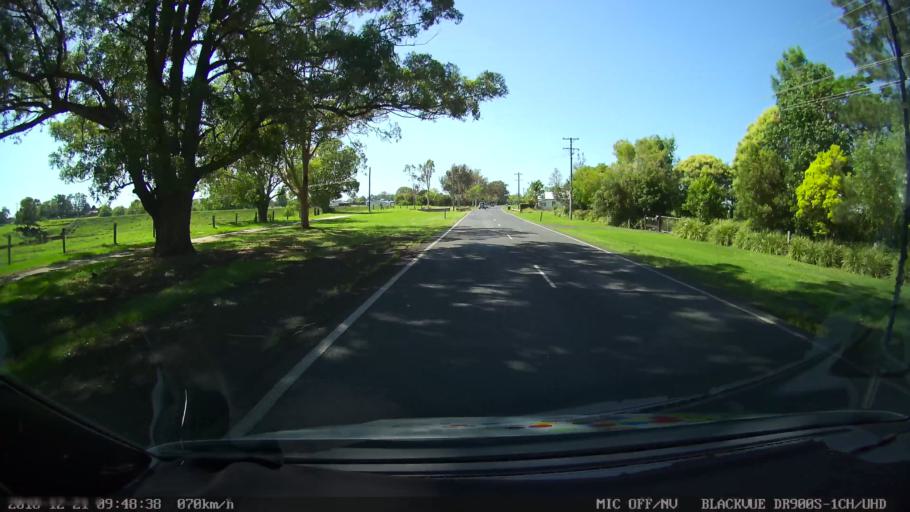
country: AU
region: New South Wales
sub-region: Clarence Valley
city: Grafton
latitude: -29.6548
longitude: 152.9347
